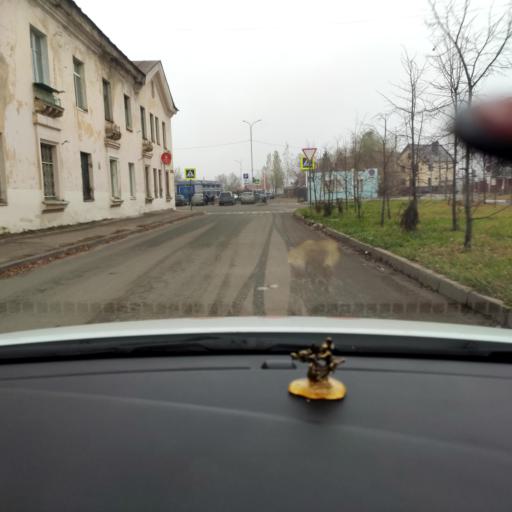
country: RU
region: Tatarstan
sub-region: Gorod Kazan'
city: Kazan
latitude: 55.7478
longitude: 49.1433
